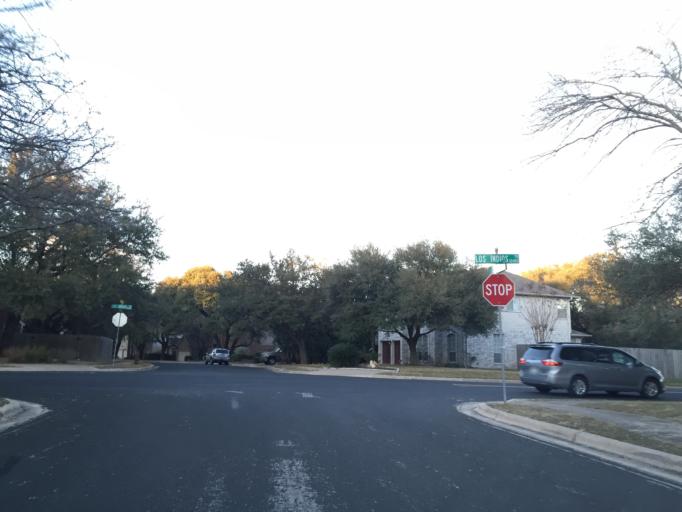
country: US
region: Texas
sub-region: Williamson County
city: Jollyville
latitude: 30.4407
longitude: -97.7628
